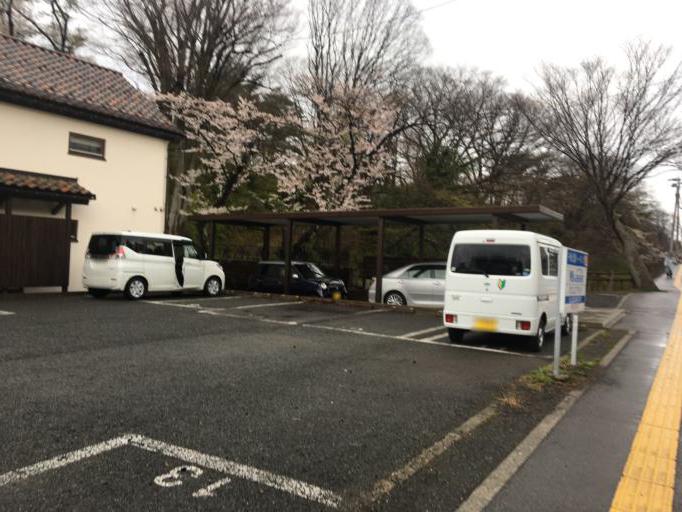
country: JP
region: Akita
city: Akita
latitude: 39.7192
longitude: 140.1254
